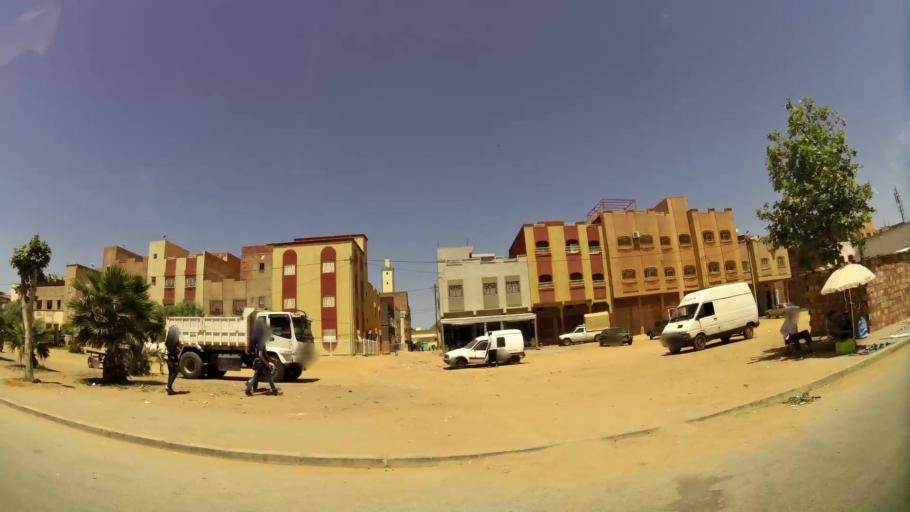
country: MA
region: Rabat-Sale-Zemmour-Zaer
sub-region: Khemisset
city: Khemisset
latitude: 33.8355
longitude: -6.0685
